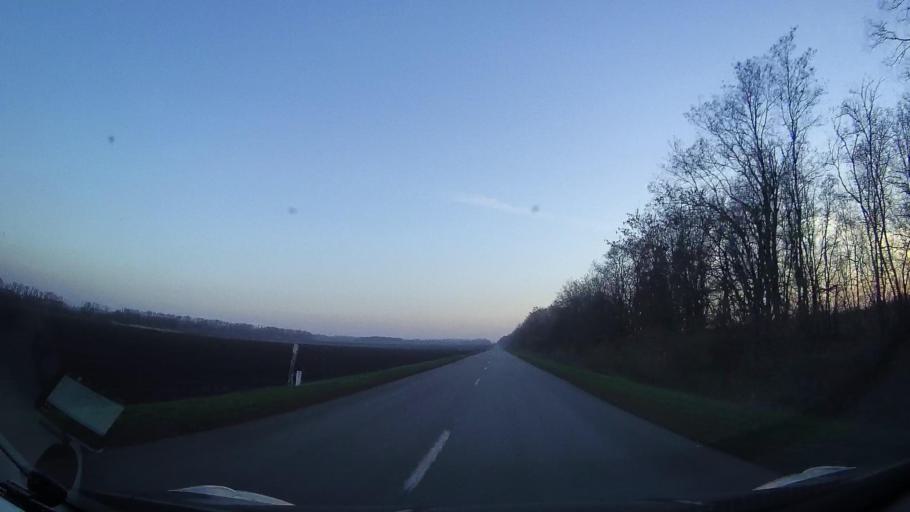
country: RU
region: Rostov
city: Zernograd
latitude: 47.0071
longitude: 40.3916
